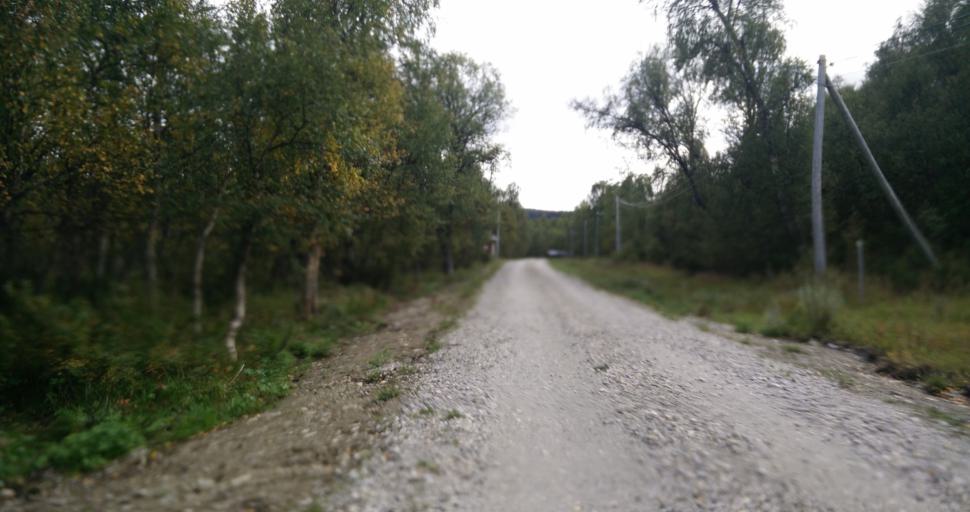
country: NO
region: Sor-Trondelag
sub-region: Tydal
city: Aas
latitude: 62.6375
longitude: 12.4182
